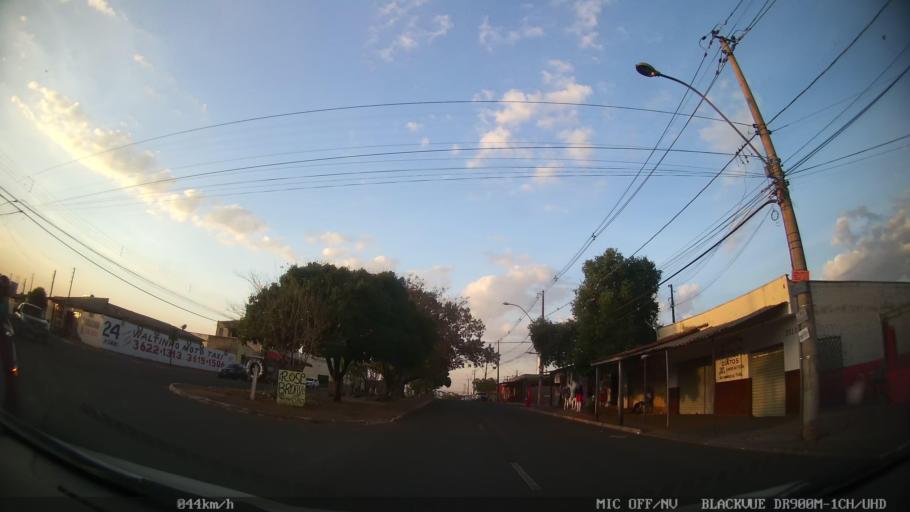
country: BR
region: Sao Paulo
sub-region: Ribeirao Preto
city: Ribeirao Preto
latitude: -21.1237
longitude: -47.8248
